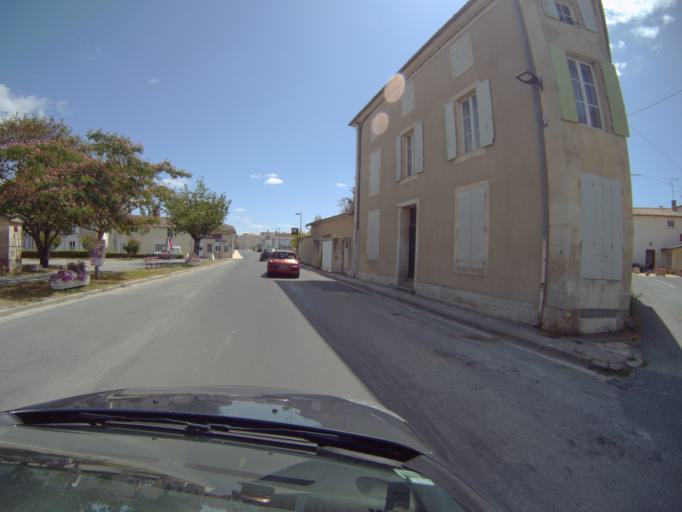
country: FR
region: Poitou-Charentes
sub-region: Departement des Deux-Sevres
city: Saint-Hilaire-la-Palud
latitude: 46.2628
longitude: -0.7119
